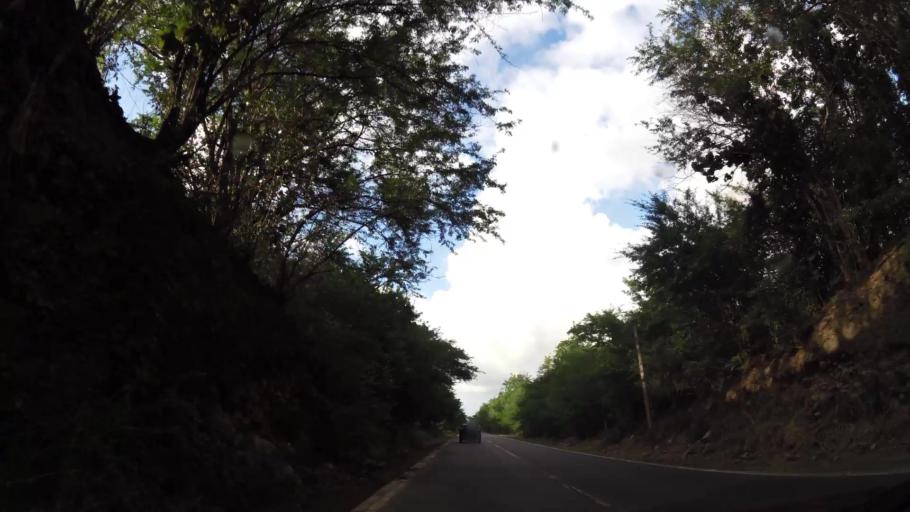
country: DM
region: Saint John
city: Portsmouth
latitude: 15.5377
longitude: -61.4747
